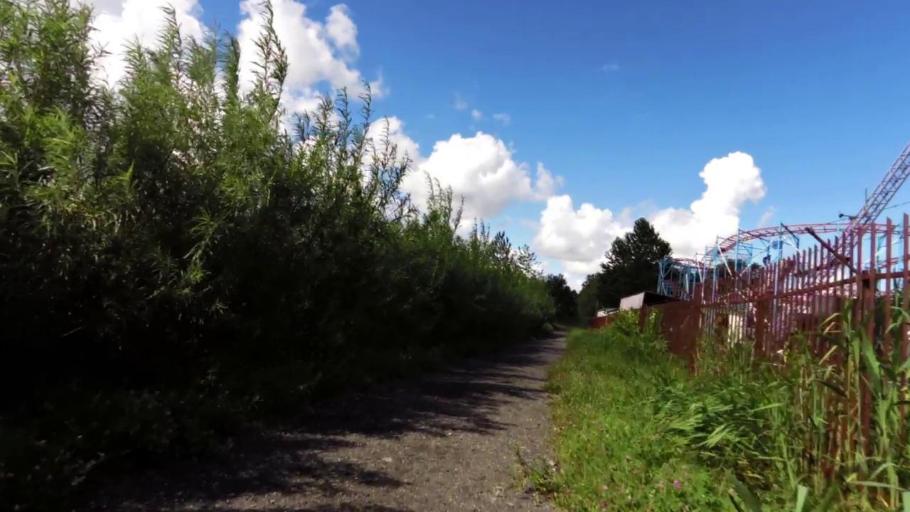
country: PL
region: West Pomeranian Voivodeship
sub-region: Powiat koszalinski
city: Mielno
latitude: 54.2590
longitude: 16.0609
